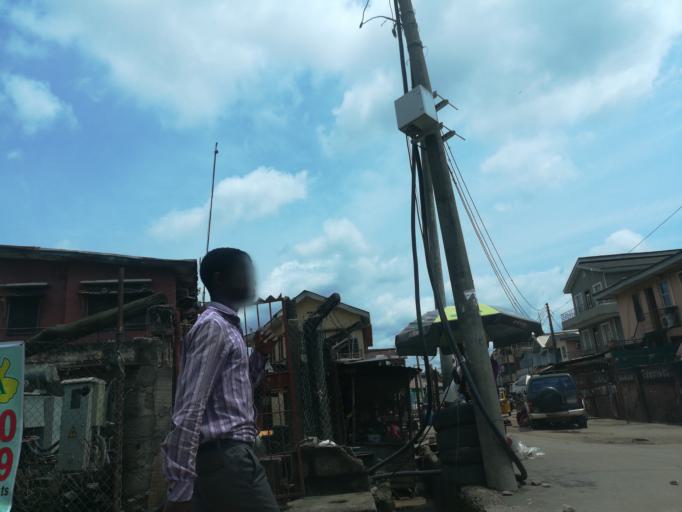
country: NG
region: Lagos
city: Somolu
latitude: 6.5392
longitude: 3.3642
